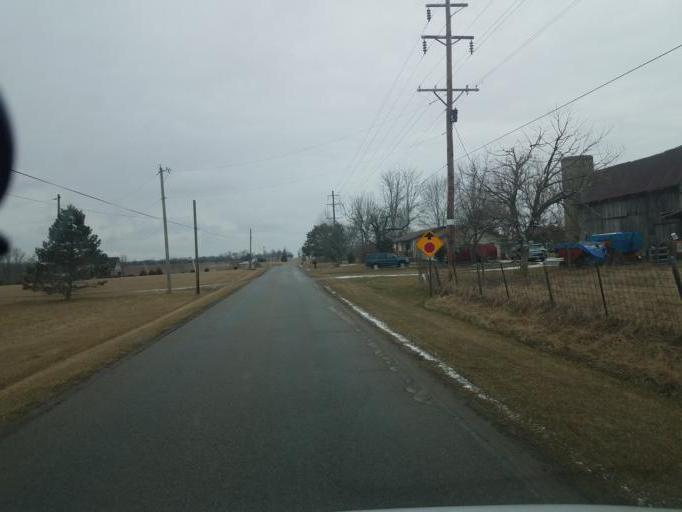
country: US
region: Ohio
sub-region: Defiance County
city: Hicksville
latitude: 41.3537
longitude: -84.7444
